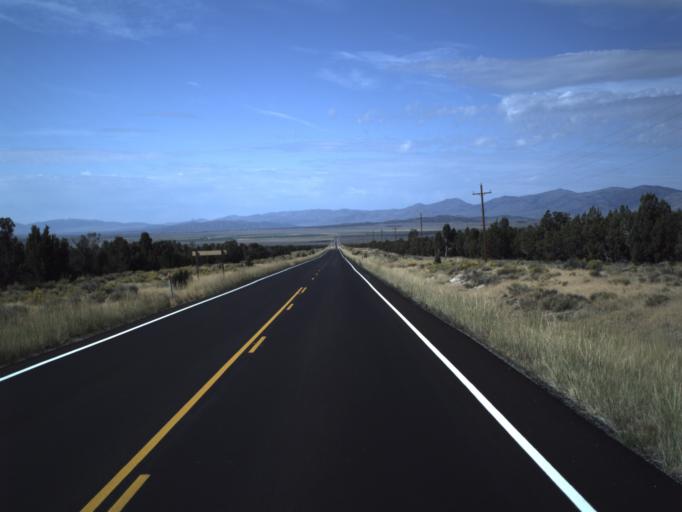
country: US
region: Idaho
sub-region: Cassia County
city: Burley
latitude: 41.8152
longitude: -113.4362
